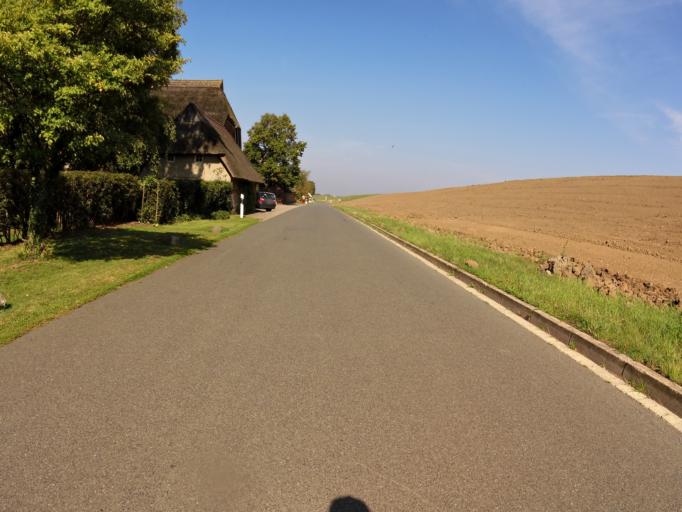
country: DE
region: Lower Saxony
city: Neuenkirchen
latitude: 53.2022
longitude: 8.4944
